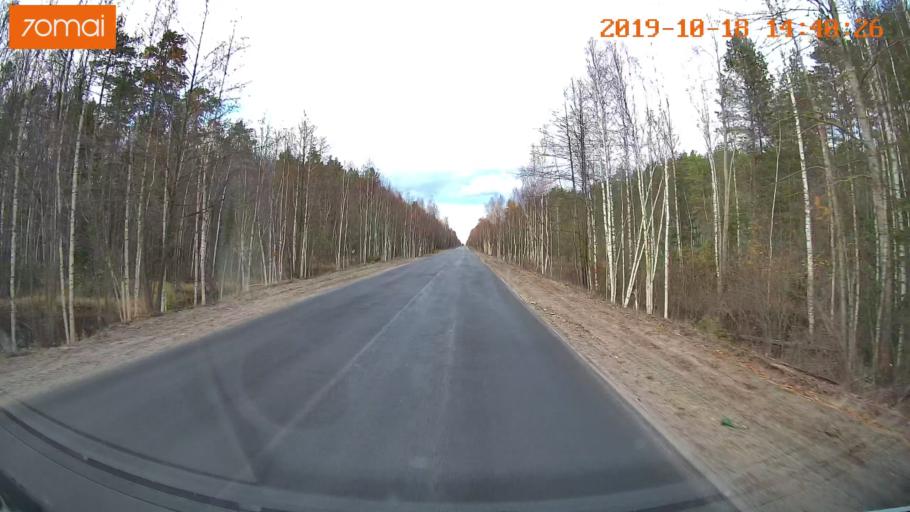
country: RU
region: Vladimir
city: Velikodvorskiy
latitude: 55.2765
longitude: 40.6690
